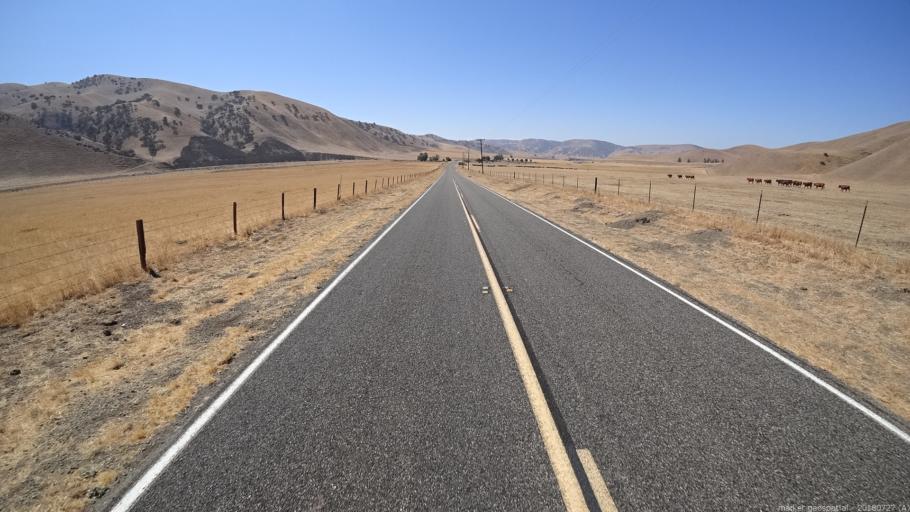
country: US
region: California
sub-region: Monterey County
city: King City
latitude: 36.3063
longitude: -120.9287
